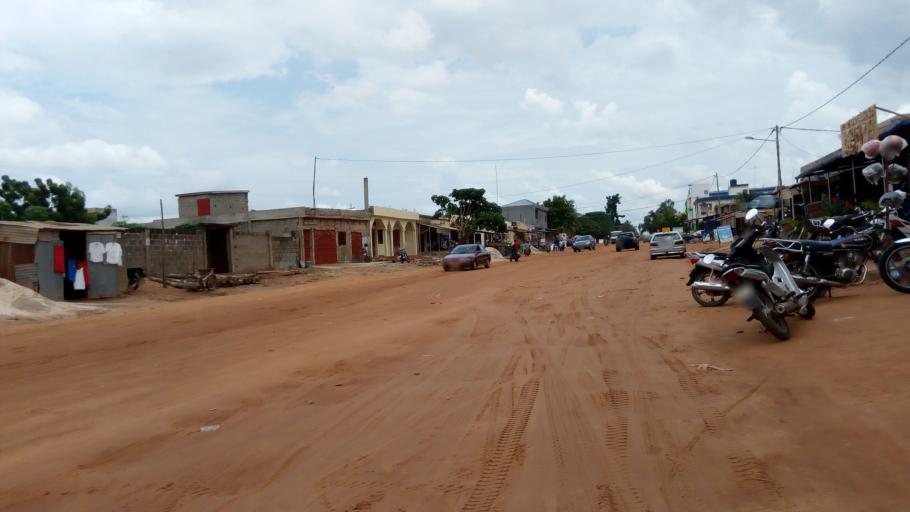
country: TG
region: Maritime
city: Lome
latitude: 6.2211
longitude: 1.1660
